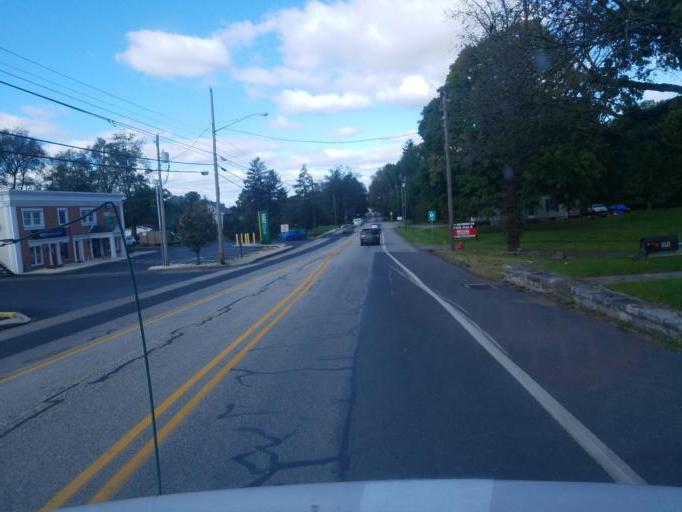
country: US
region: Pennsylvania
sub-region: Franklin County
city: Greencastle
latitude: 39.7871
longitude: -77.7152
